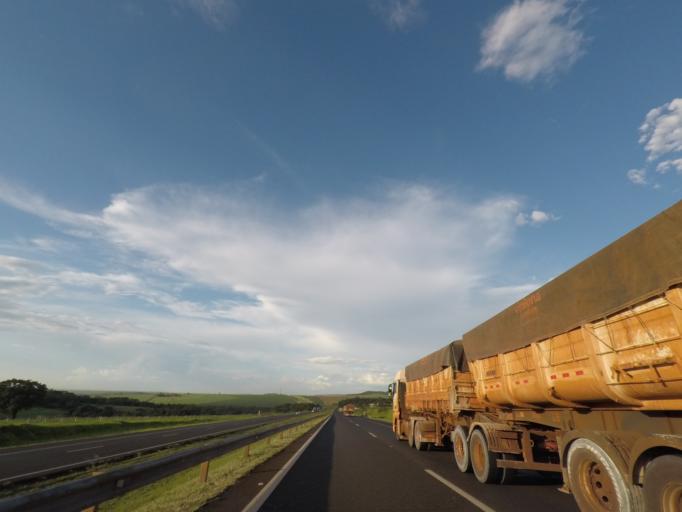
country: BR
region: Sao Paulo
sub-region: Ituverava
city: Ituverava
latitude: -20.2996
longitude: -47.7994
